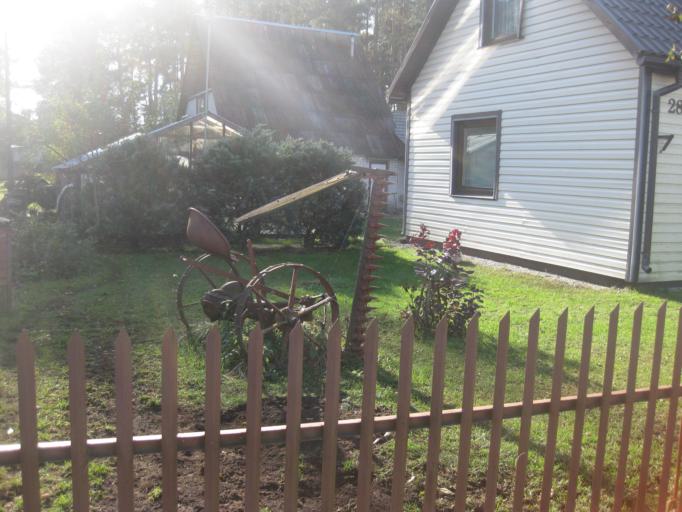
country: LT
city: Ezerelis
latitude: 54.8844
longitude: 23.5967
